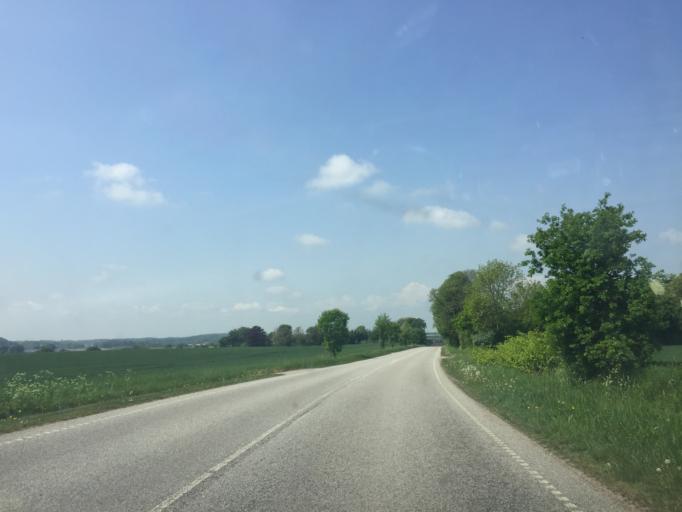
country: DK
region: South Denmark
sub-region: Kolding Kommune
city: Sonder Bjert
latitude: 55.3735
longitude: 9.5917
